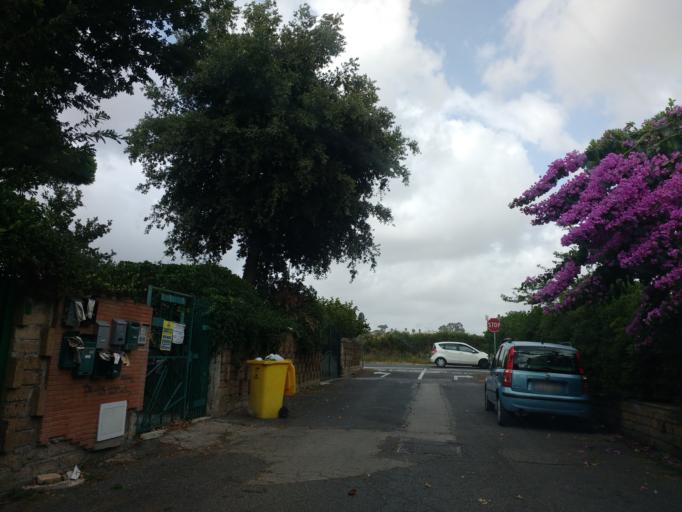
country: IT
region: Latium
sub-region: Citta metropolitana di Roma Capitale
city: Lavinio
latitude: 41.4930
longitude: 12.5939
